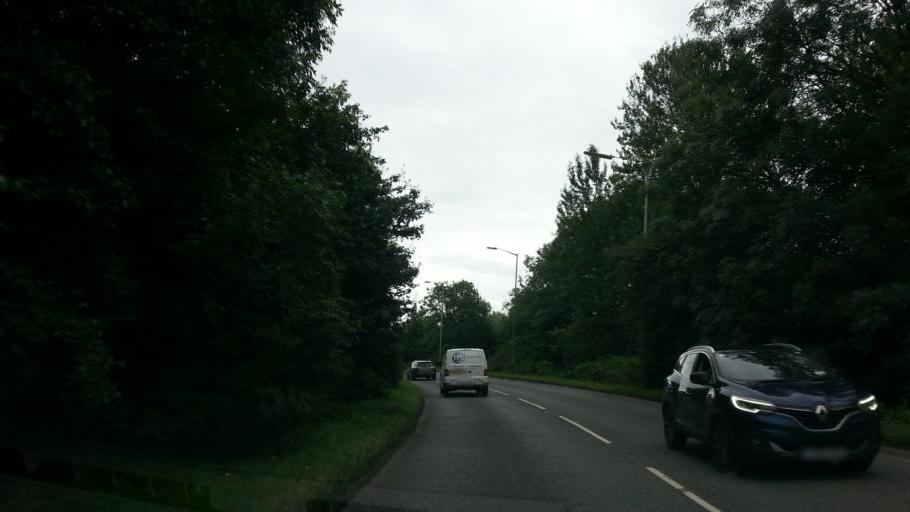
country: GB
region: England
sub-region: Wiltshire
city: Melksham
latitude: 51.3664
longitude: -2.1453
